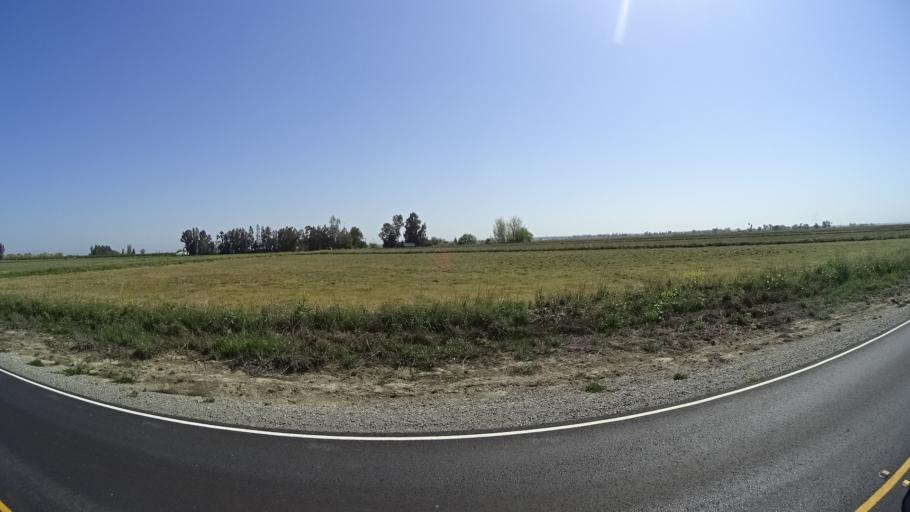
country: US
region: California
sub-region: Glenn County
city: Willows
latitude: 39.5936
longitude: -122.0655
